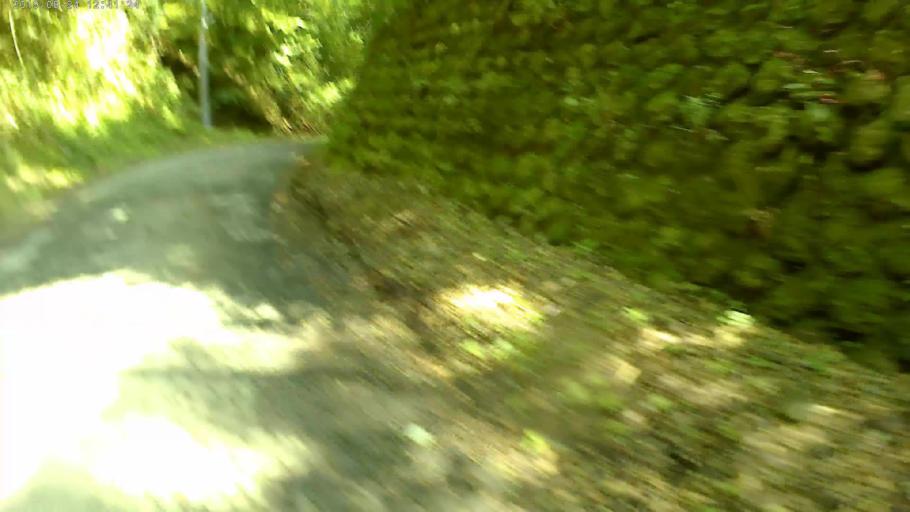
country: JP
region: Nagano
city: Komoro
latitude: 36.2665
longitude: 138.3688
